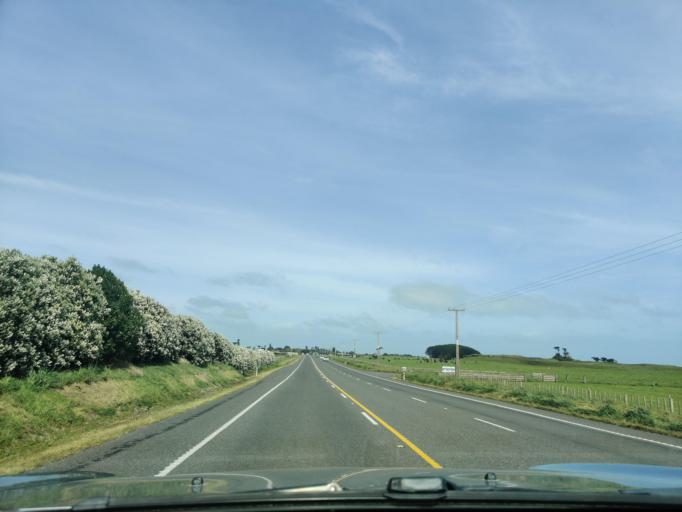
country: NZ
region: Taranaki
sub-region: South Taranaki District
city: Patea
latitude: -39.7381
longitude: 174.4563
